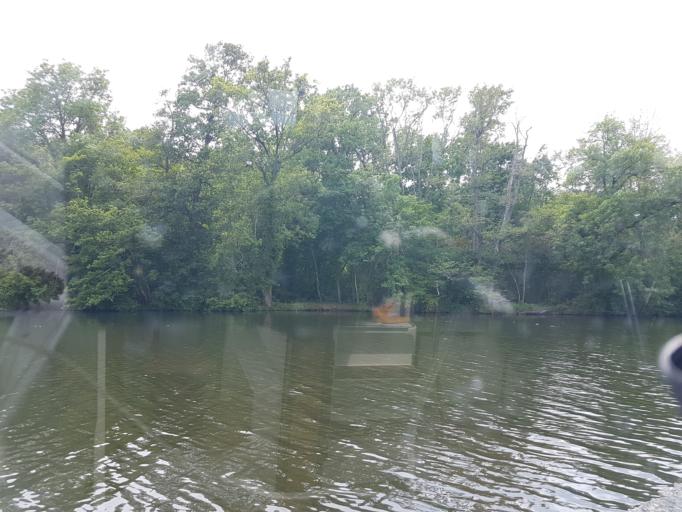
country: FR
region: Bourgogne
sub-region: Departement de l'Yonne
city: Gurgy
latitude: 47.8611
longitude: 3.5525
